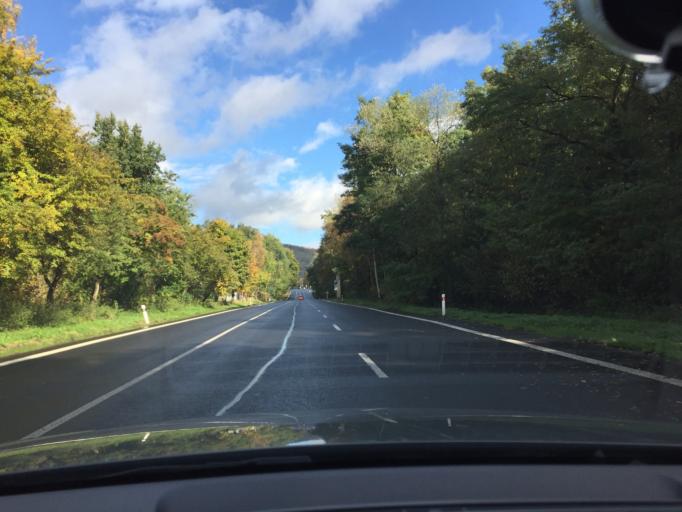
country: CZ
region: Ustecky
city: Chlumec
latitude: 50.7089
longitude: 13.9537
